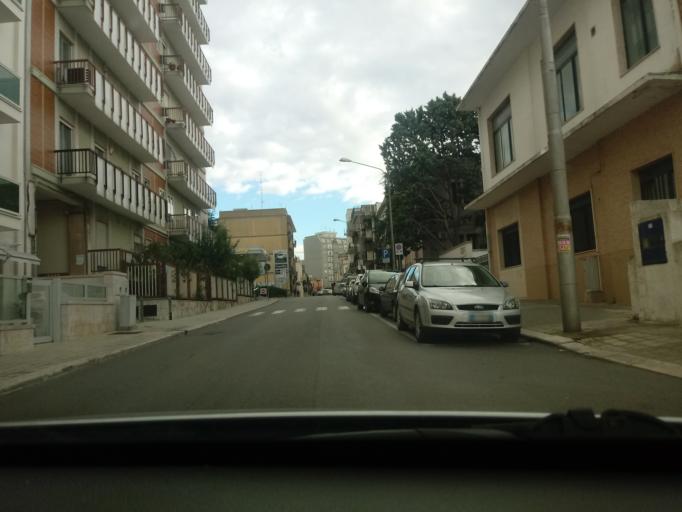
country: IT
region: Apulia
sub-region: Provincia di Bari
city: Putignano
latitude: 40.8535
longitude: 17.1172
